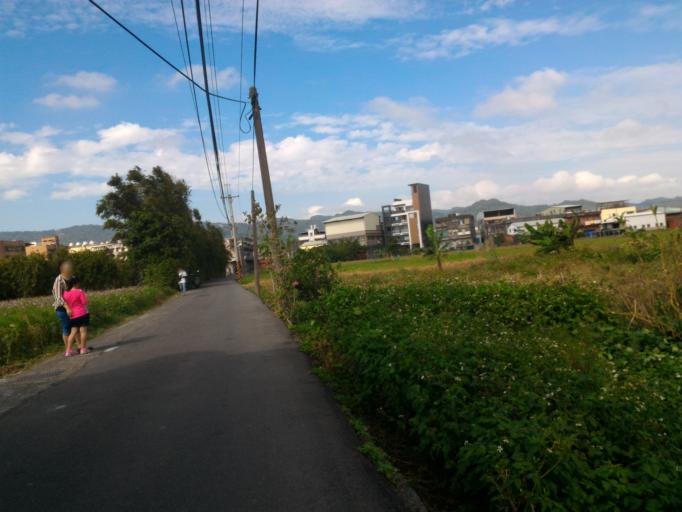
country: TW
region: Taiwan
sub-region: Taoyuan
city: Taoyuan
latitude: 24.9543
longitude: 121.3933
